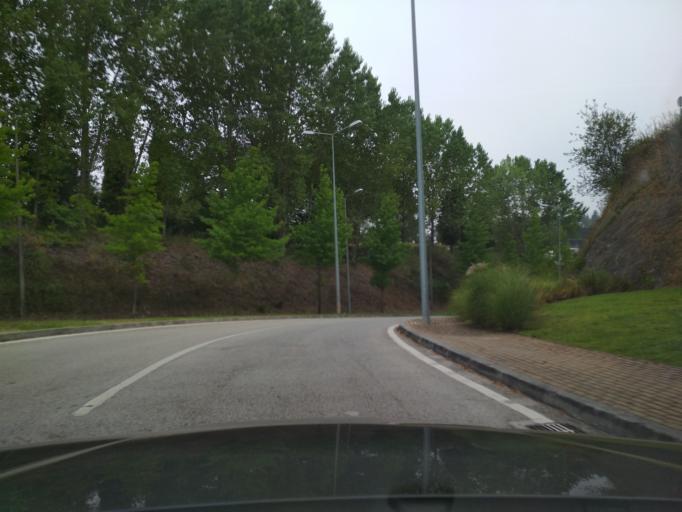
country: PT
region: Coimbra
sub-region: Coimbra
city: Coimbra
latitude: 40.2226
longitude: -8.4153
